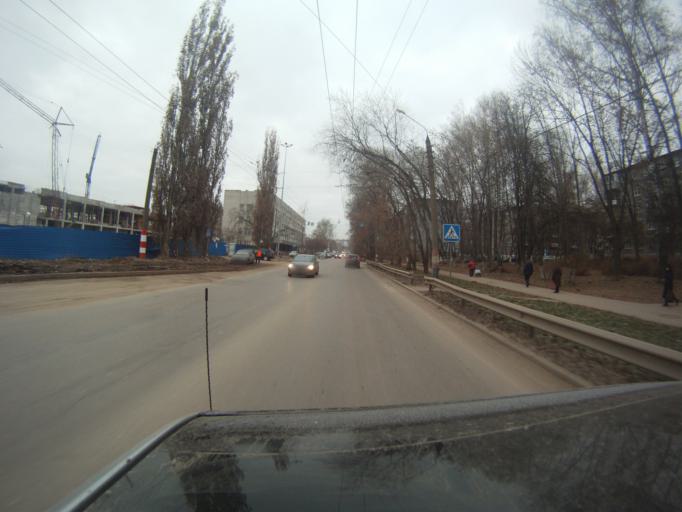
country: RU
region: Nizjnij Novgorod
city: Nizhniy Novgorod
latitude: 56.2976
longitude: 44.0421
